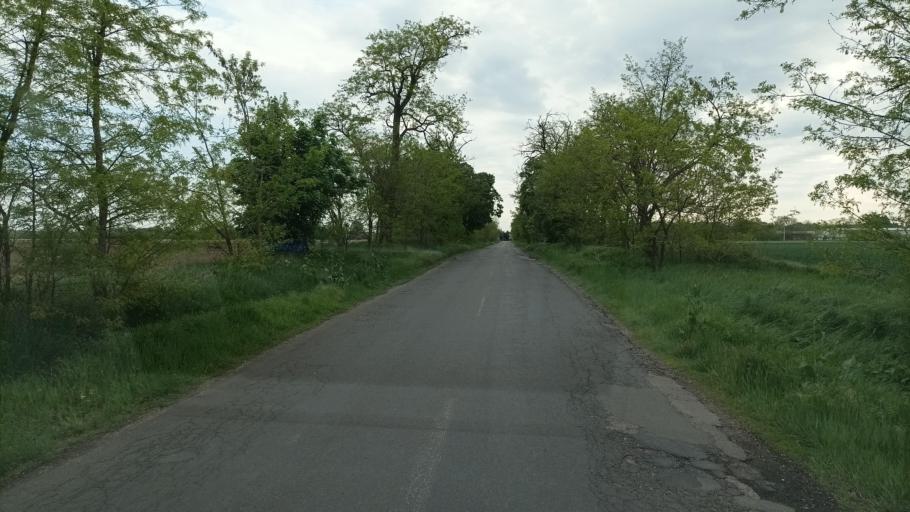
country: HU
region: Pest
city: Nyaregyhaza
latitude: 47.2705
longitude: 19.5190
